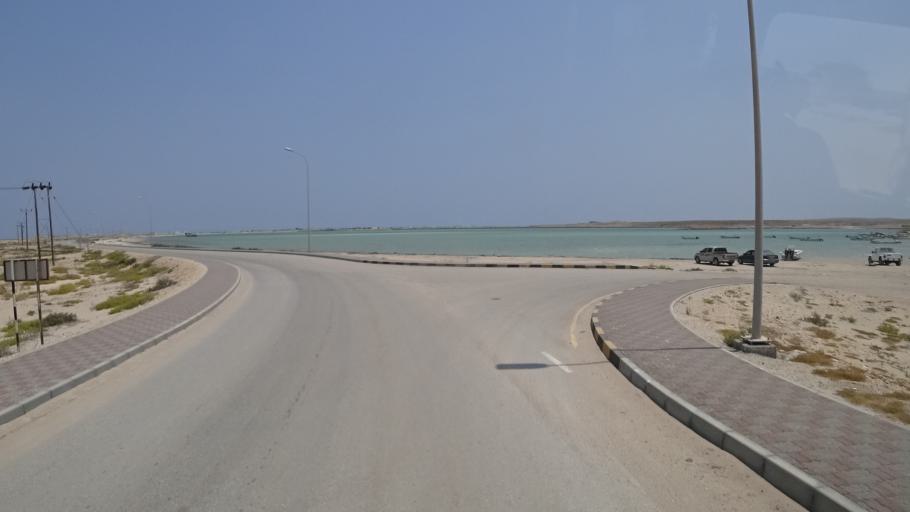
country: OM
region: Ash Sharqiyah
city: Sur
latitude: 22.5279
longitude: 59.7648
